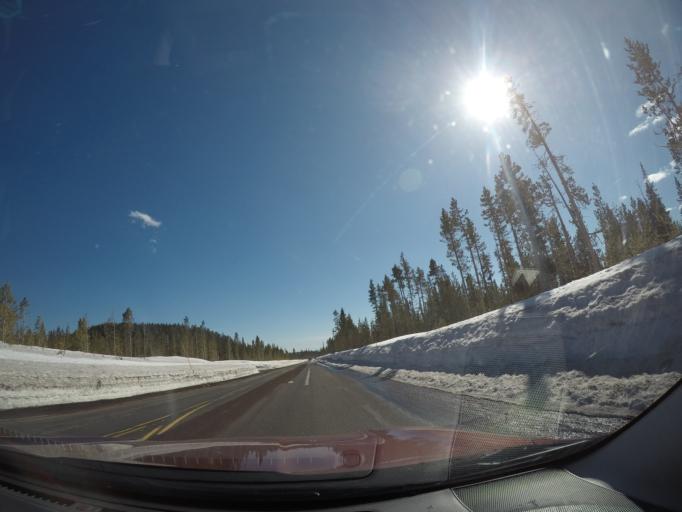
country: US
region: Oregon
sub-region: Deschutes County
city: Sunriver
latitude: 43.9795
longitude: -121.6123
